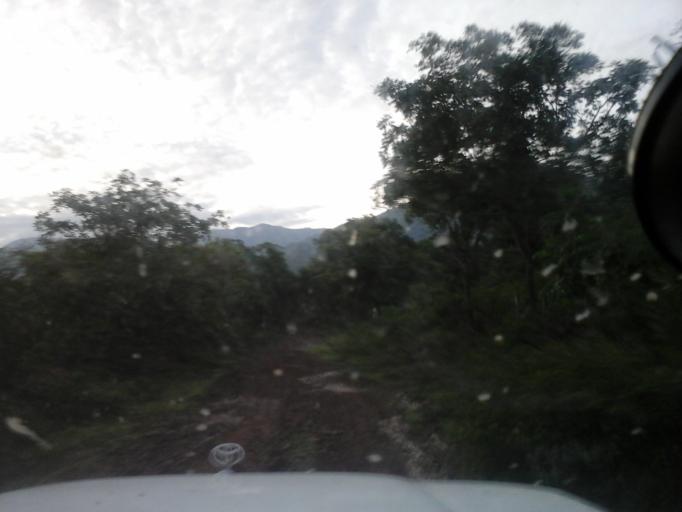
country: CO
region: Cesar
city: Agustin Codazzi
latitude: 10.1711
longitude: -73.1740
